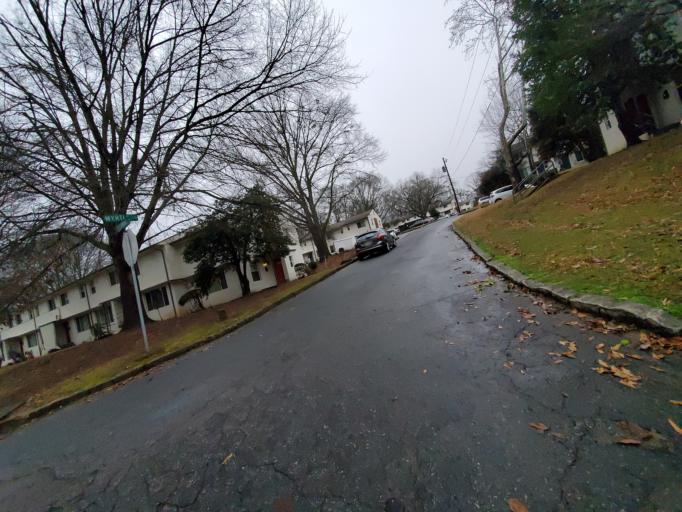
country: US
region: Georgia
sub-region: DeKalb County
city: North Decatur
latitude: 33.7929
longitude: -84.3023
